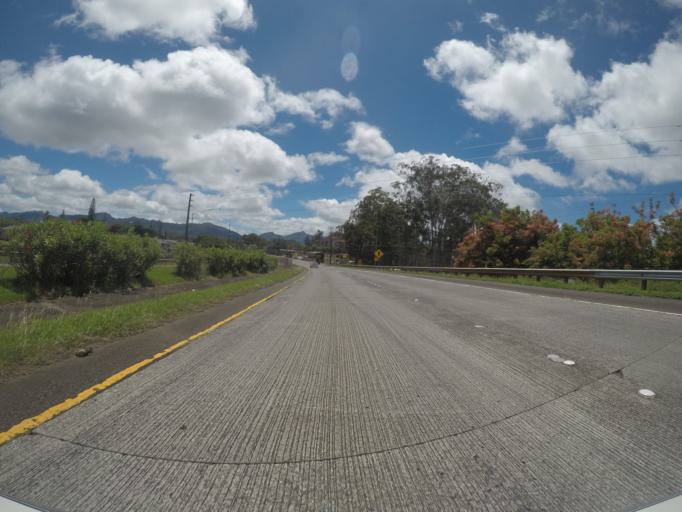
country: US
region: Hawaii
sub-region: Honolulu County
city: Wahiawa
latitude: 21.4904
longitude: -158.0303
